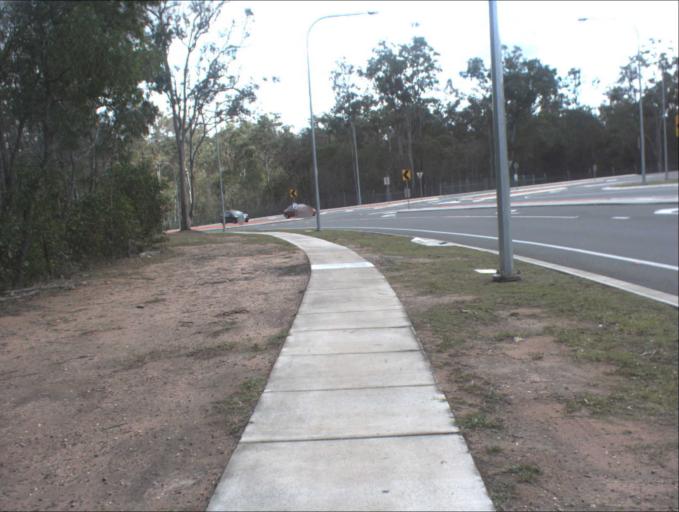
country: AU
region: Queensland
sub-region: Logan
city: Park Ridge South
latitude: -27.7065
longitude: 152.9756
